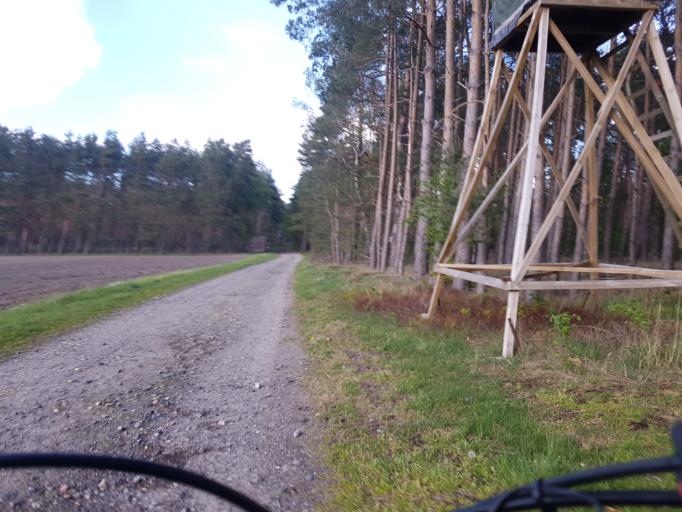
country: DE
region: Brandenburg
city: Trobitz
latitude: 51.5646
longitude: 13.4279
